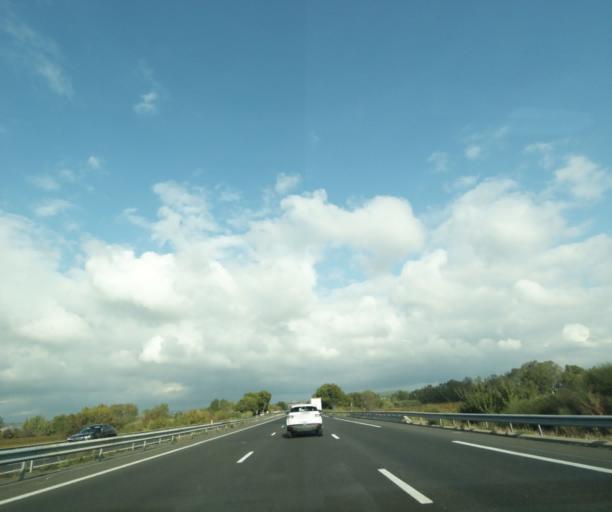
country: FR
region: Languedoc-Roussillon
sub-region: Departement de l'Aude
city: Fleury
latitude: 43.2430
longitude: 3.1485
